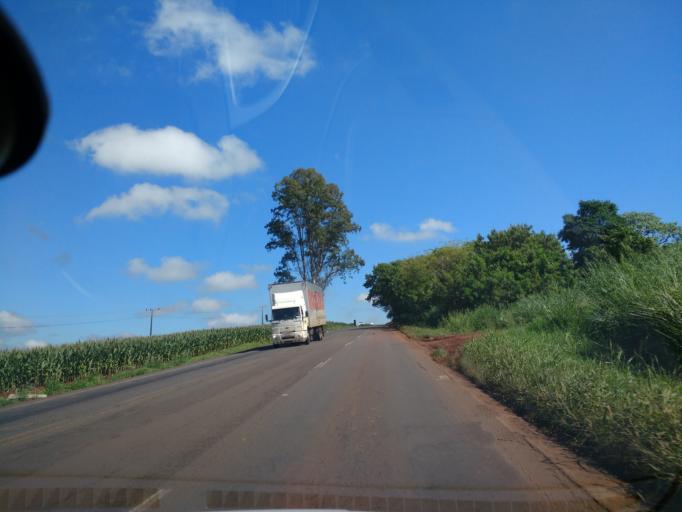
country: BR
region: Parana
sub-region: Cianorte
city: Cianorte
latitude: -23.6545
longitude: -52.5190
